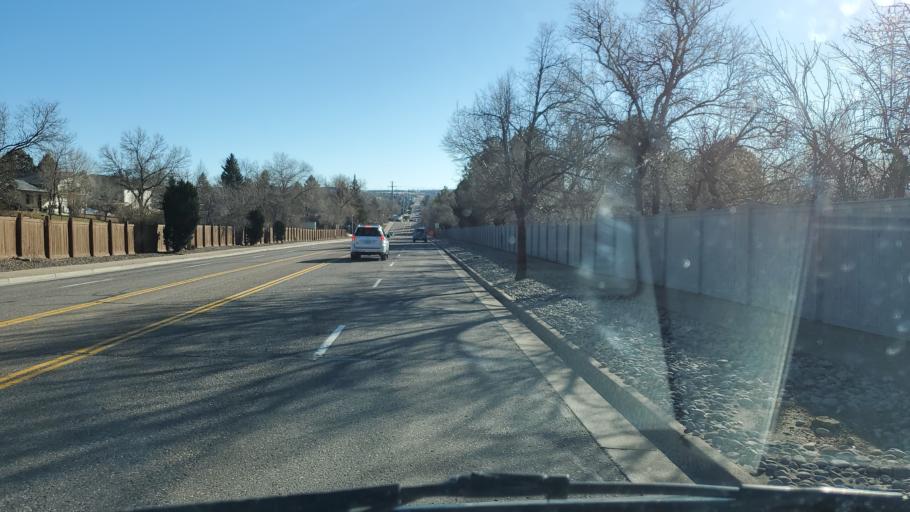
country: US
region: Colorado
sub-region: Arapahoe County
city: Castlewood
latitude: 39.5849
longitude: -104.9043
